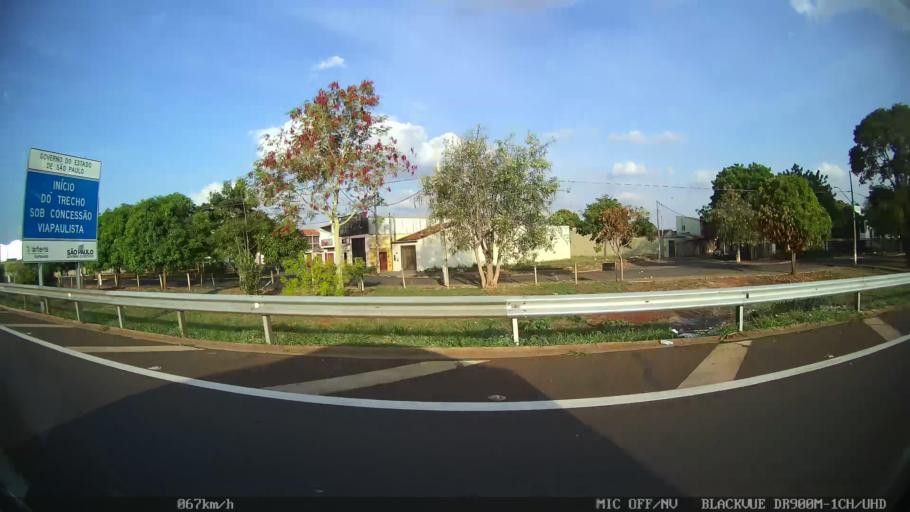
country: BR
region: Sao Paulo
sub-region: Ribeirao Preto
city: Ribeirao Preto
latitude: -21.1166
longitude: -47.7839
